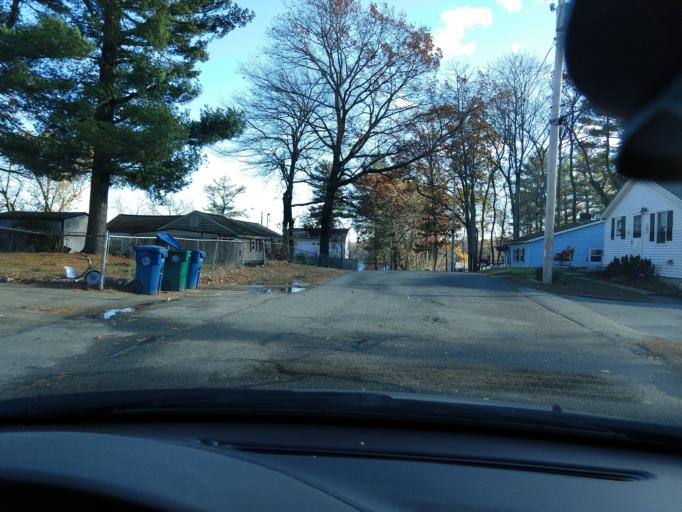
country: US
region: Massachusetts
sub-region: Middlesex County
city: Billerica
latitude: 42.5379
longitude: -71.2739
